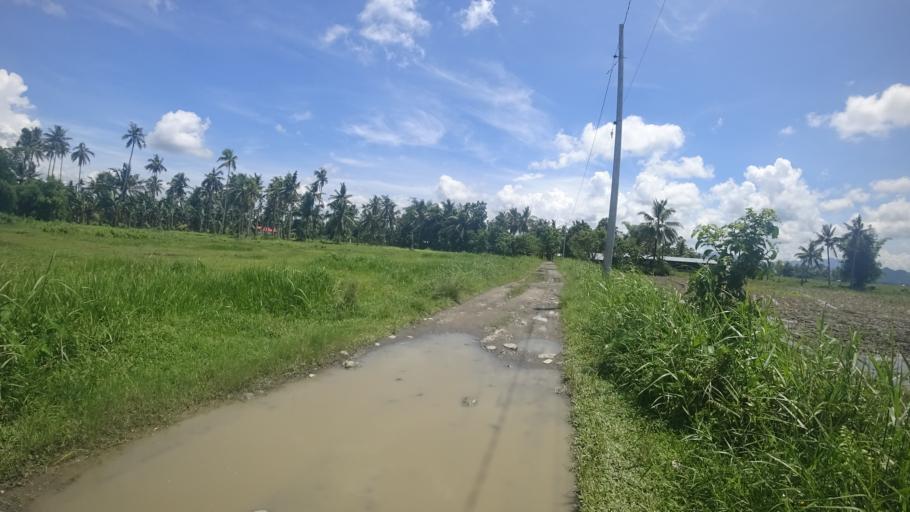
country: PH
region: Eastern Visayas
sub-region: Province of Leyte
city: Alangalang
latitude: 11.2320
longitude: 124.8447
